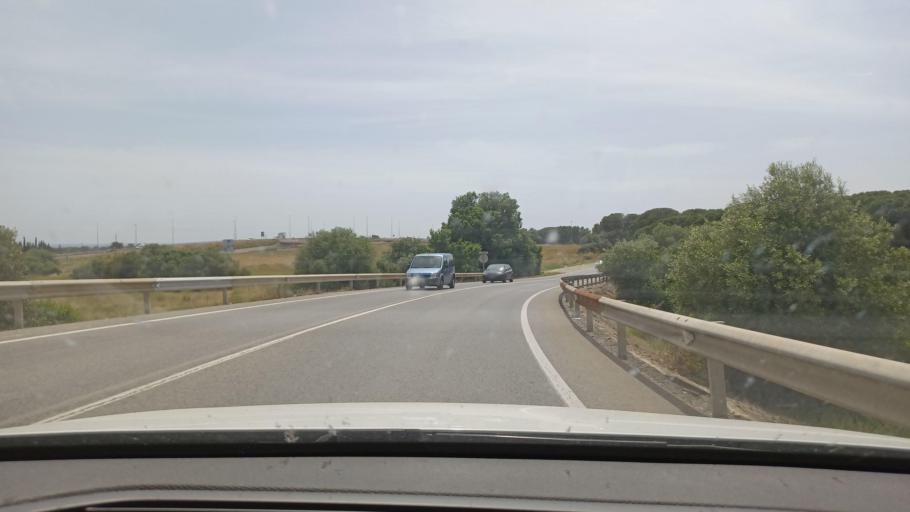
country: ES
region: Catalonia
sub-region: Provincia de Tarragona
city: Cambrils
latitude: 41.0868
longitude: 1.0798
